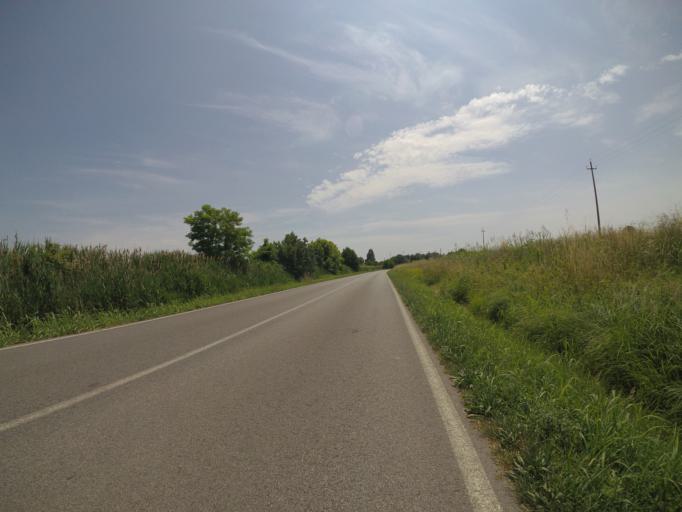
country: IT
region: Friuli Venezia Giulia
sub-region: Provincia di Udine
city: Teor
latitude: 45.8763
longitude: 13.0880
